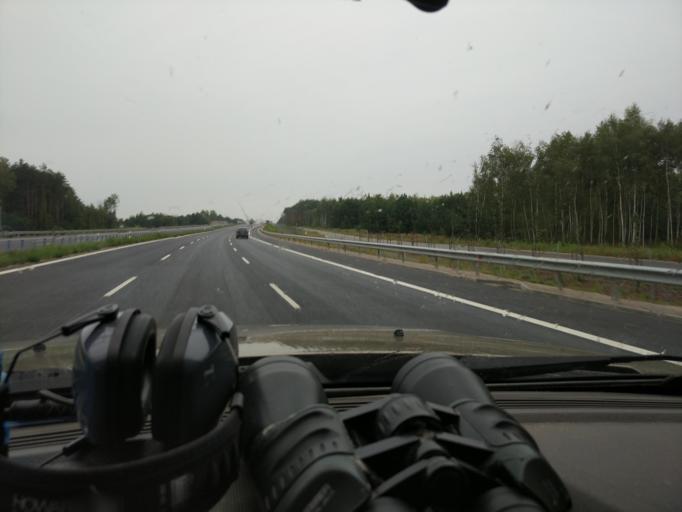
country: PL
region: Masovian Voivodeship
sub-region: Powiat wolominski
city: Slupno
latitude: 52.3803
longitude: 21.1893
